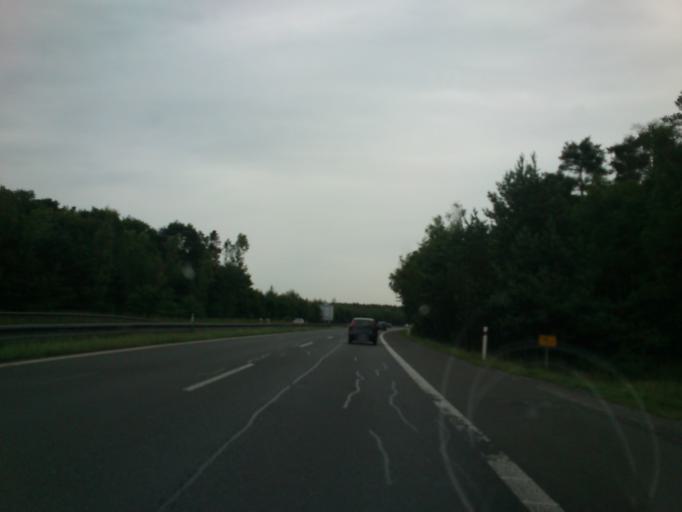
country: CZ
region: Central Bohemia
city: Brandys nad Labem-Stara Boleslav
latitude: 50.2099
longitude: 14.6990
